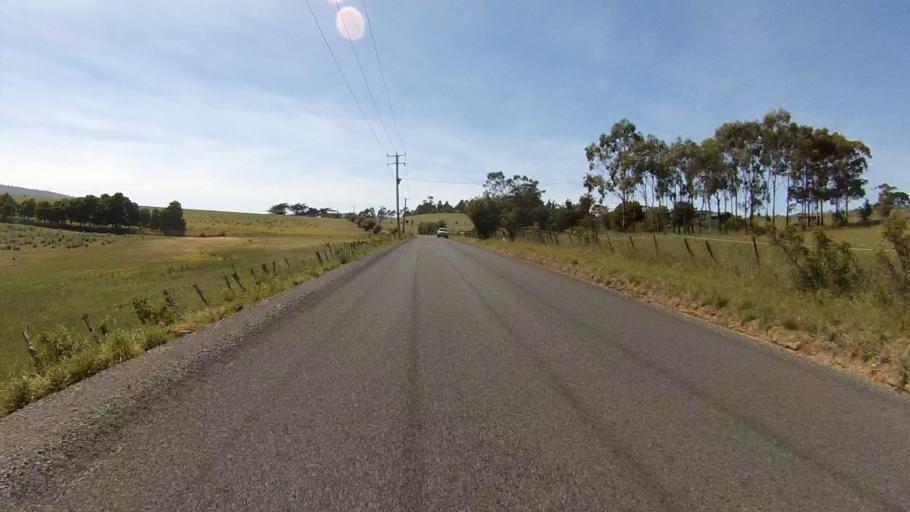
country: AU
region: Tasmania
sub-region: Sorell
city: Sorell
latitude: -42.7635
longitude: 147.6302
